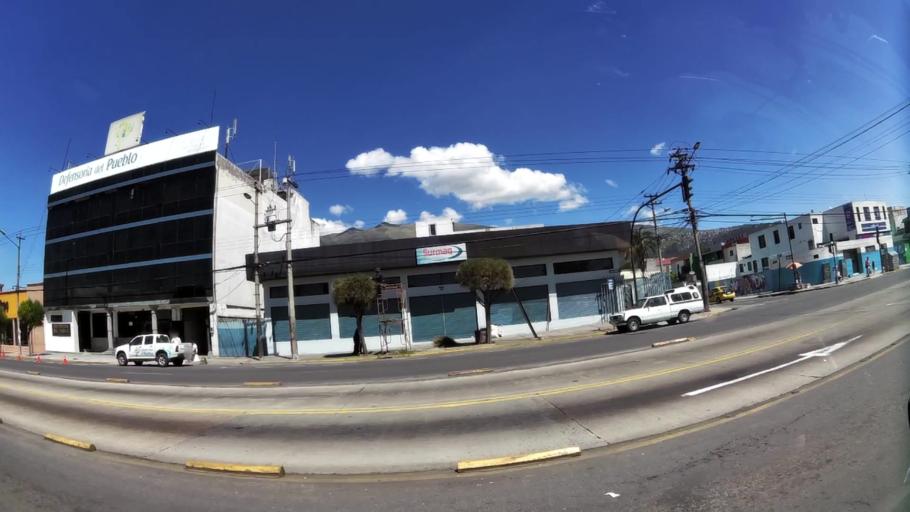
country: EC
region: Pichincha
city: Quito
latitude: -0.1391
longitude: -78.4929
